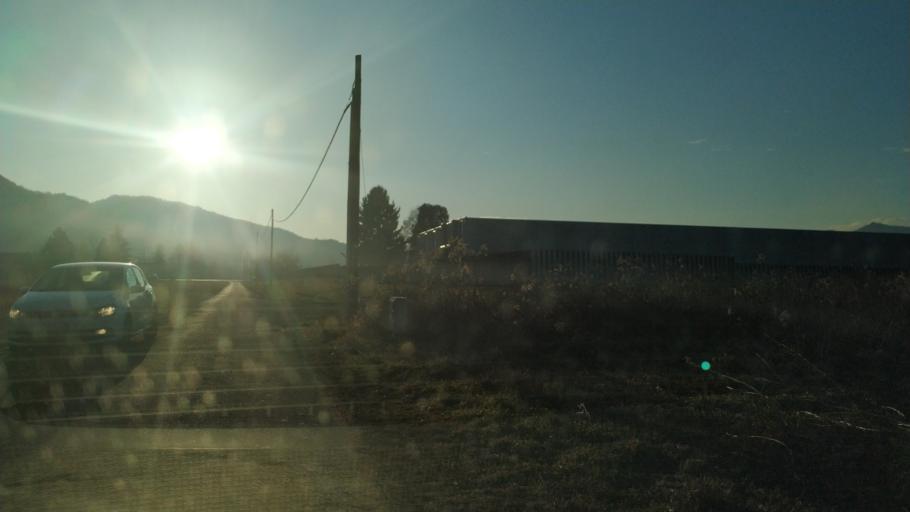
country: IT
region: Piedmont
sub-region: Provincia di Novara
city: Prato Sesia
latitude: 45.6612
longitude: 8.3604
